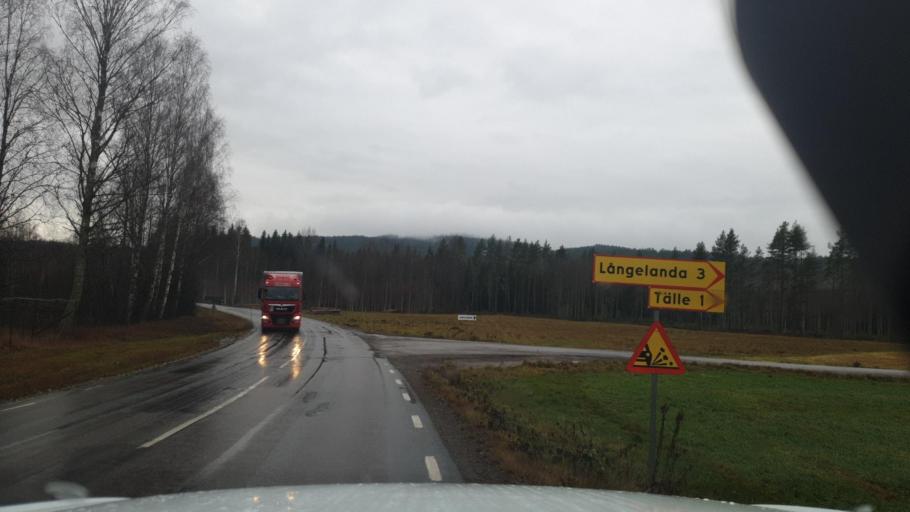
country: SE
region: Vaermland
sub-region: Eda Kommun
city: Charlottenberg
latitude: 59.8364
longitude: 12.2707
